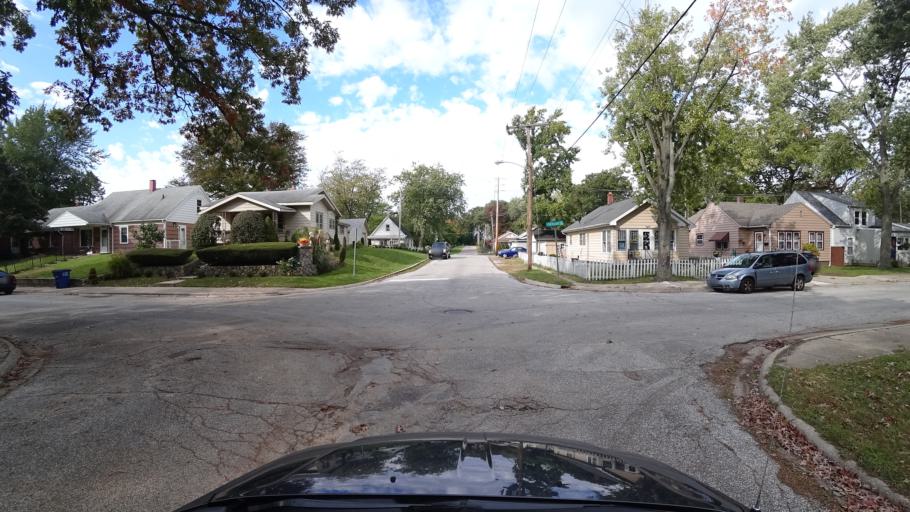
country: US
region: Indiana
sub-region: LaPorte County
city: Michigan City
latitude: 41.7048
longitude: -86.8783
